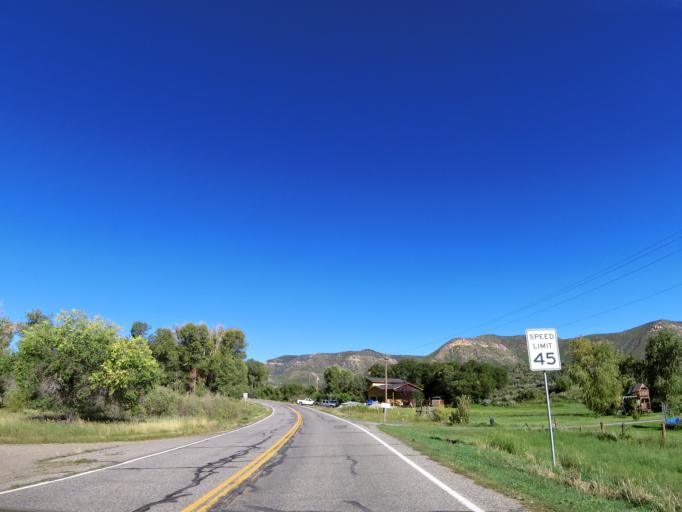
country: US
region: Colorado
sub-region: Montezuma County
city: Mancos
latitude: 37.3444
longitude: -108.2849
